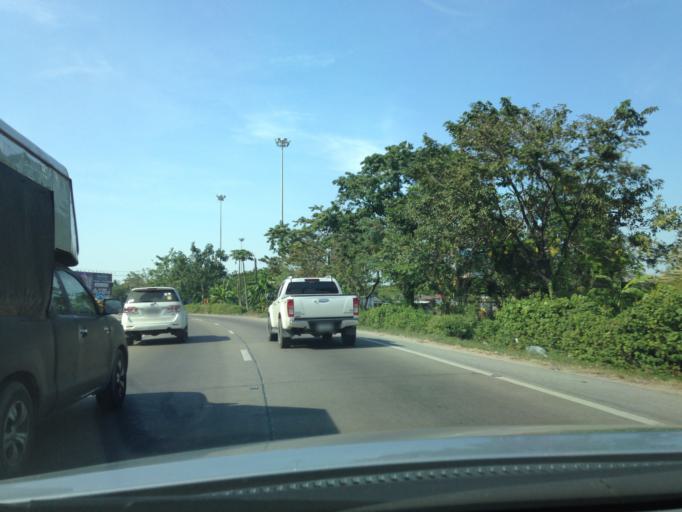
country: TH
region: Nonthaburi
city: Bang Bua Thong
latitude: 13.8707
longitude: 100.4098
